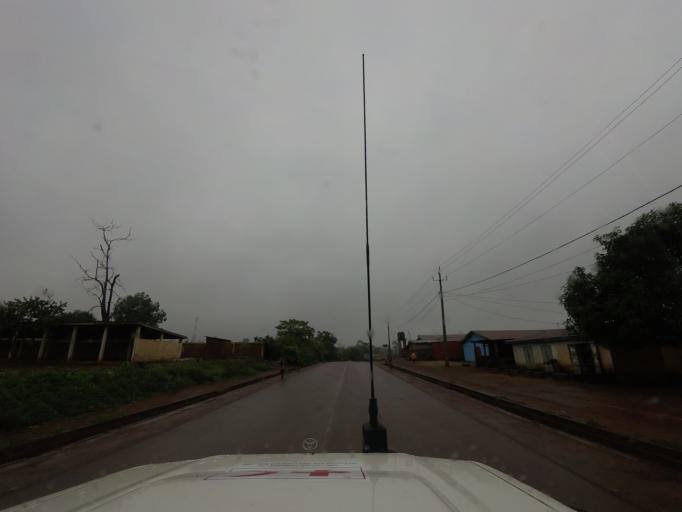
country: GN
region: Nzerekore
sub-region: Nzerekore Prefecture
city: Nzerekore
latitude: 7.7336
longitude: -8.8300
